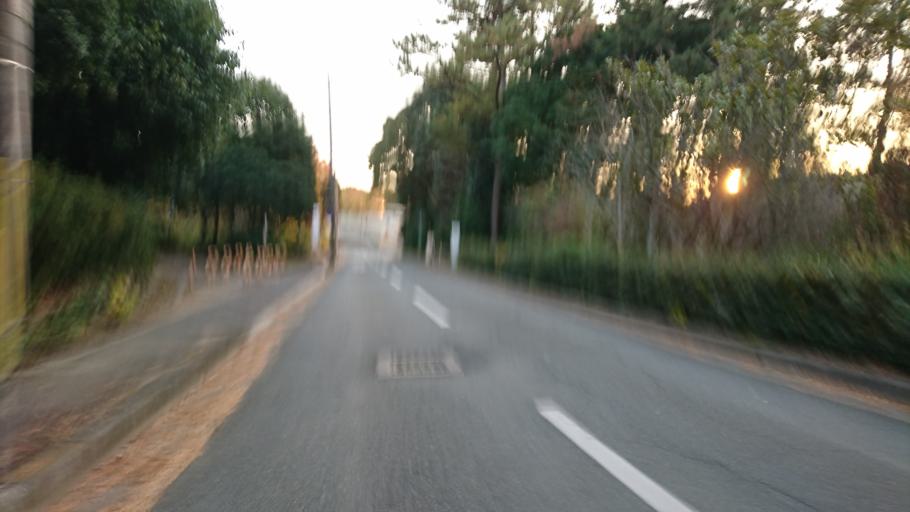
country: JP
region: Hyogo
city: Kakogawacho-honmachi
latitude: 34.7764
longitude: 134.8626
